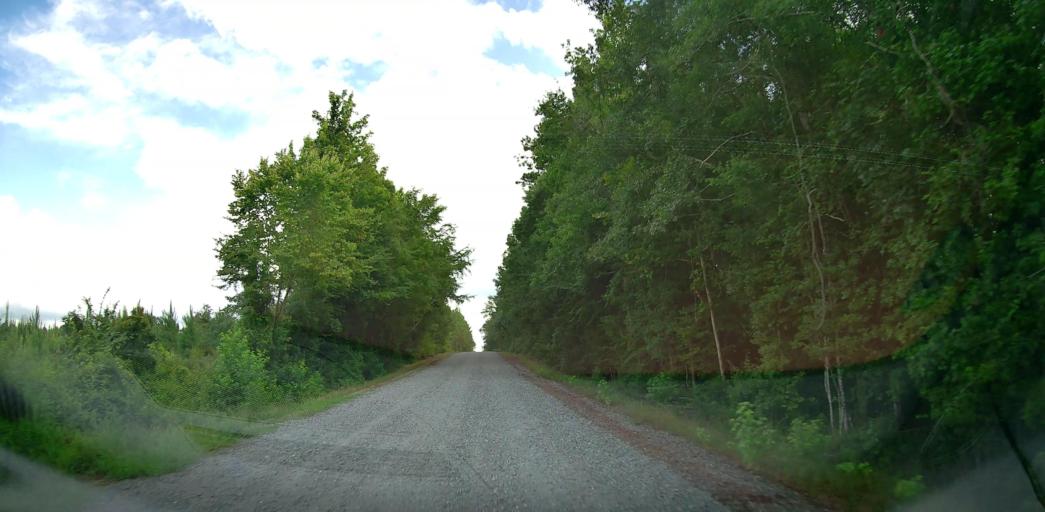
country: US
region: Georgia
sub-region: Bleckley County
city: Cochran
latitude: 32.4243
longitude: -83.4539
